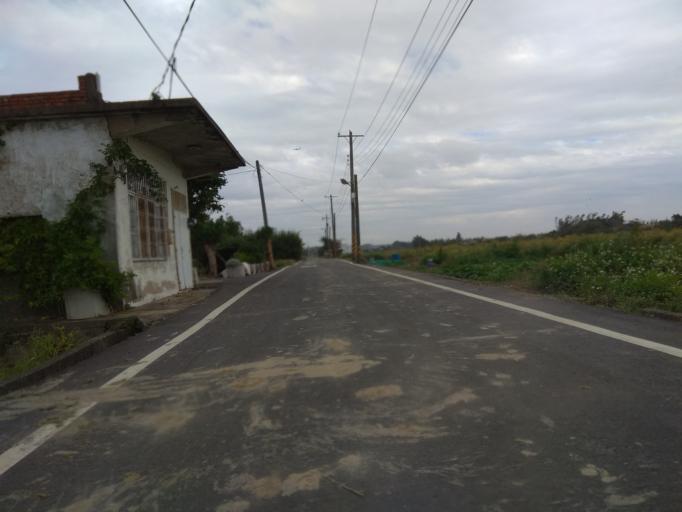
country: TW
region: Taiwan
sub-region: Hsinchu
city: Zhubei
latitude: 24.9849
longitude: 121.0470
